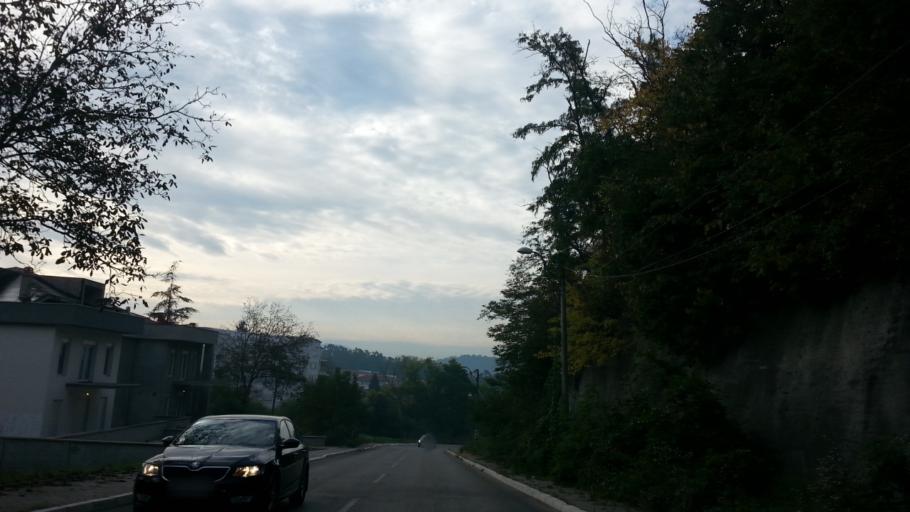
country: RS
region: Central Serbia
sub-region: Belgrade
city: Savski Venac
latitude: 44.7656
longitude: 20.4565
